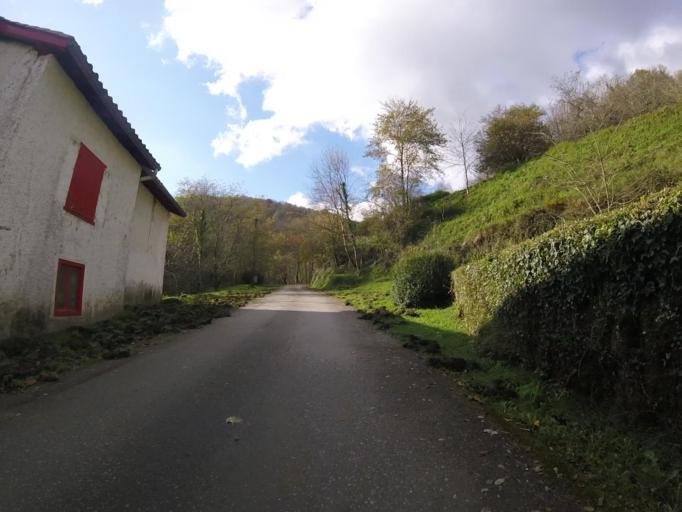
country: ES
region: Navarre
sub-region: Provincia de Navarra
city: Arantza
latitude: 43.2131
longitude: -1.7968
